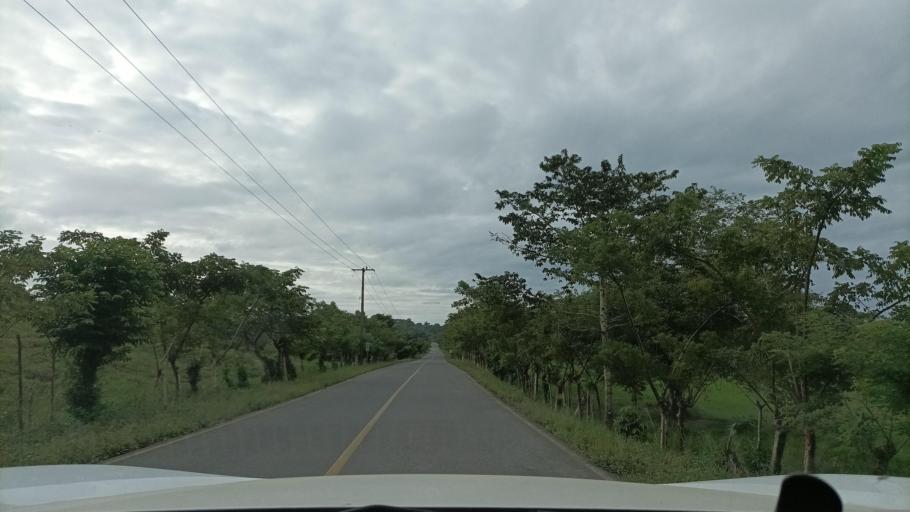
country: MX
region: Veracruz
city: Hidalgotitlan
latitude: 17.6926
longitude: -94.4689
